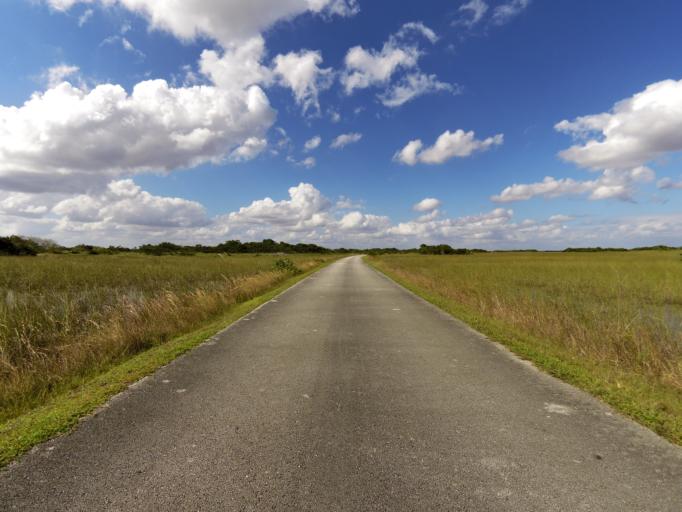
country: US
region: Florida
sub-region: Miami-Dade County
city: The Hammocks
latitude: 25.6961
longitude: -80.7617
